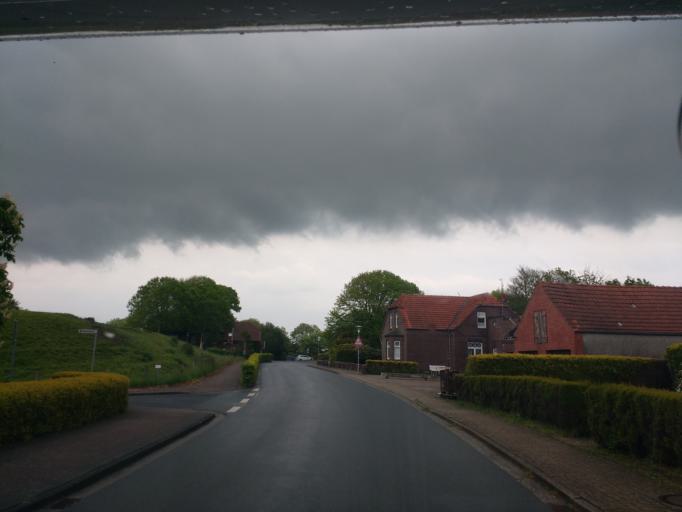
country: DE
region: Lower Saxony
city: Wangerooge
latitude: 53.6988
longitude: 7.8984
